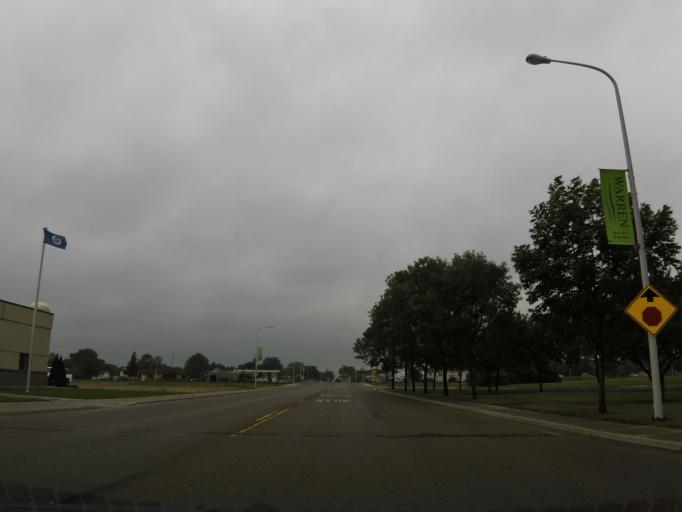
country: US
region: Minnesota
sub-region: Marshall County
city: Warren
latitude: 48.1951
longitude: -96.7692
